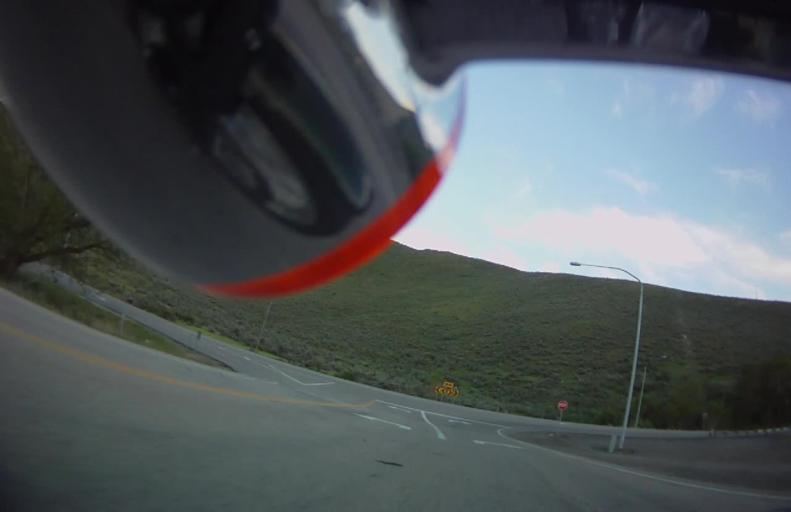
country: US
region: Utah
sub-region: Wasatch County
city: Midway
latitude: 40.4561
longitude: -111.4716
